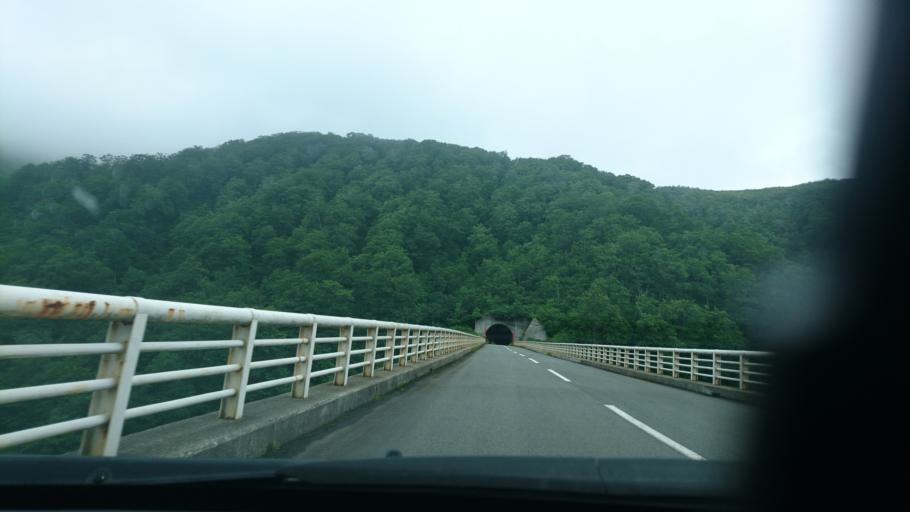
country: JP
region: Akita
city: Yuzawa
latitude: 39.1491
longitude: 140.7677
